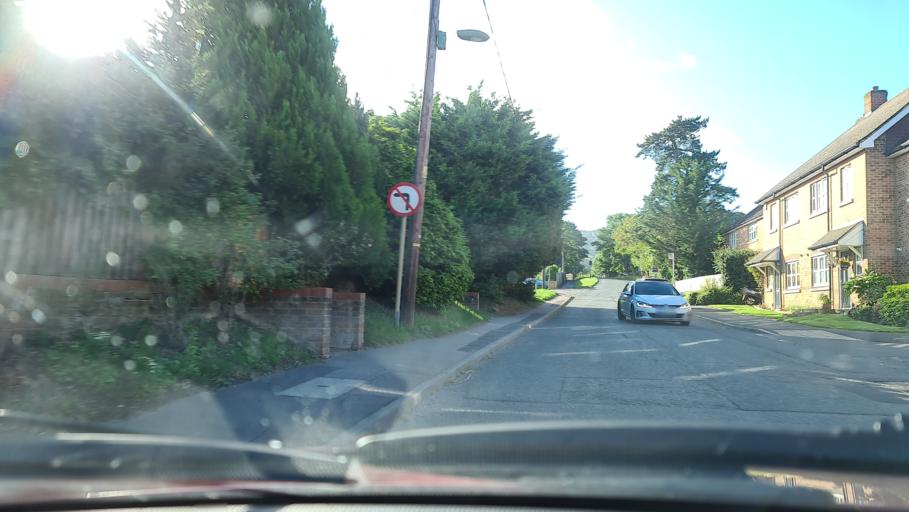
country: GB
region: England
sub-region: Oxfordshire
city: Chinnor
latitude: 51.6998
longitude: -0.9067
